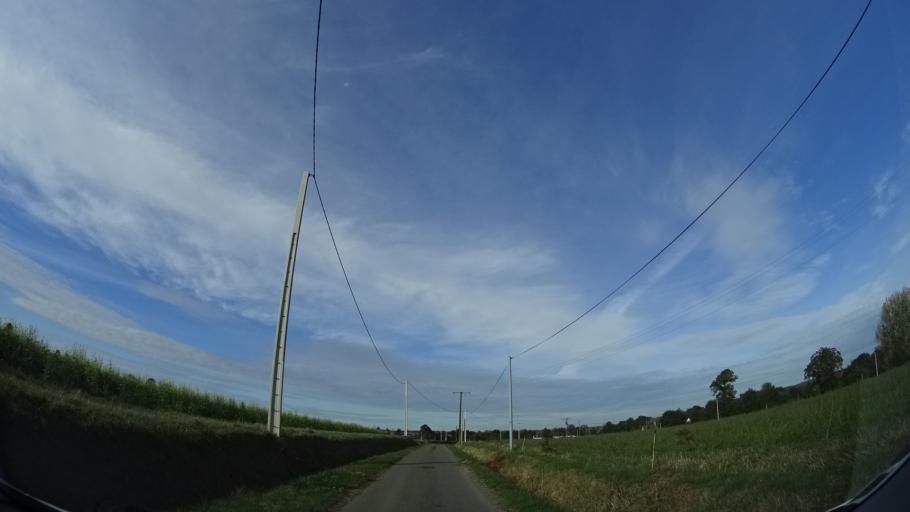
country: FR
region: Brittany
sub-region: Departement d'Ille-et-Vilaine
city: Geveze
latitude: 48.2377
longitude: -1.8287
